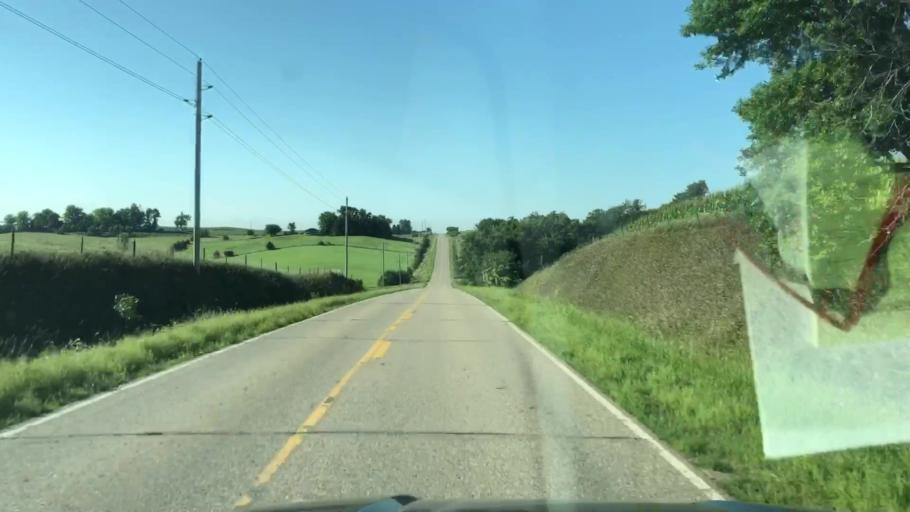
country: US
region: Iowa
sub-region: Woodbury County
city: Sergeant Bluff
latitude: 42.4359
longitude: -96.2136
